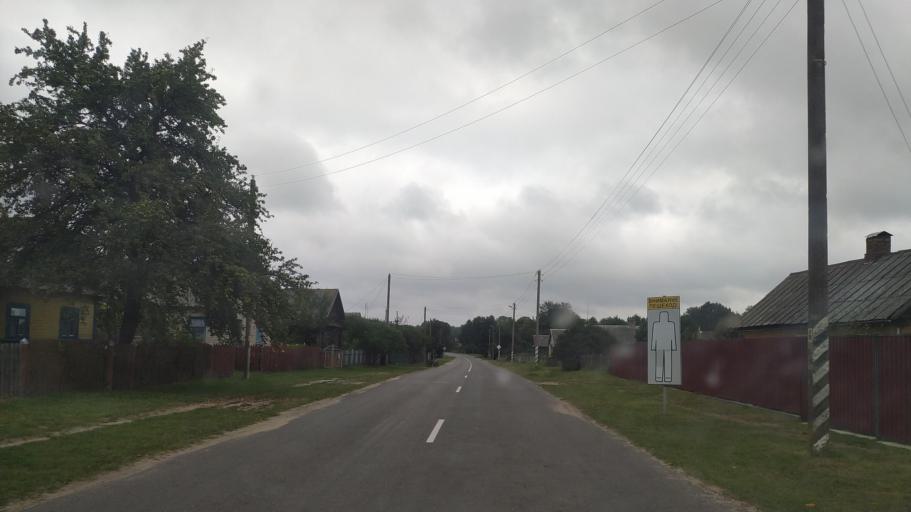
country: BY
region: Brest
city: Byaroza
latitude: 52.5904
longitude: 24.8707
